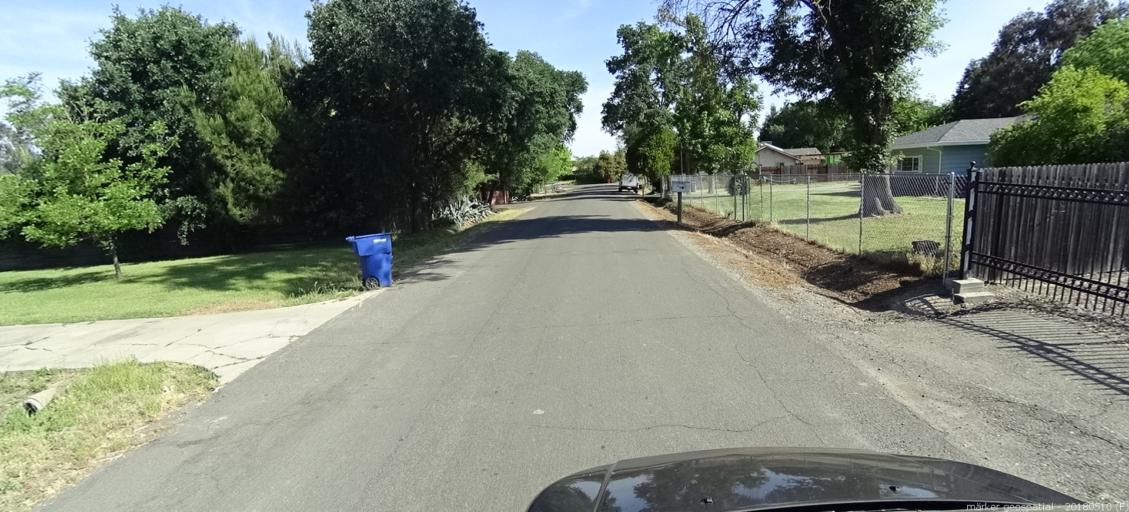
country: US
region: California
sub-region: Sacramento County
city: Rio Linda
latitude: 38.6618
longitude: -121.4810
